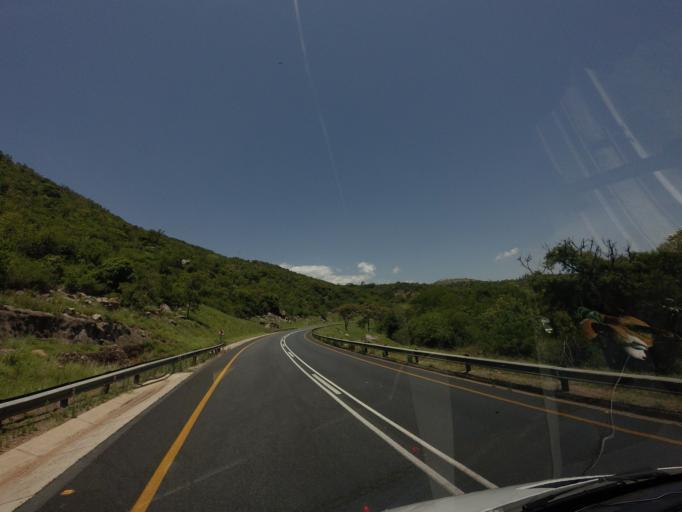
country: ZA
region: Mpumalanga
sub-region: Ehlanzeni District
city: Nelspruit
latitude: -25.4588
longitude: 30.6964
